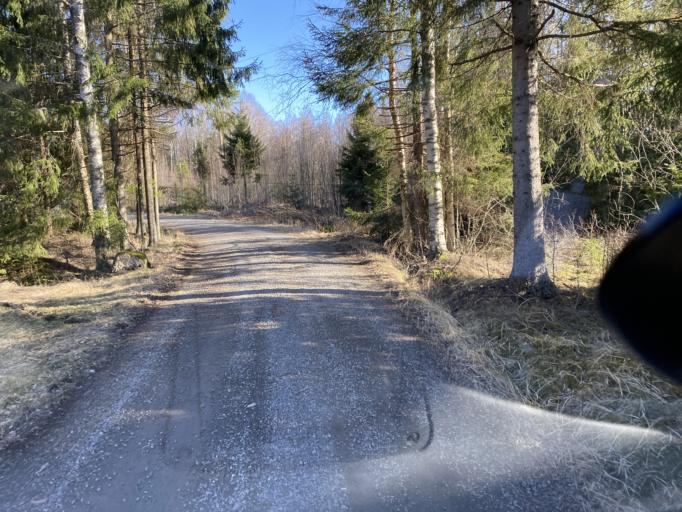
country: FI
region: Satakunta
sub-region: Rauma
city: Lappi
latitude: 61.1503
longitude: 21.8804
